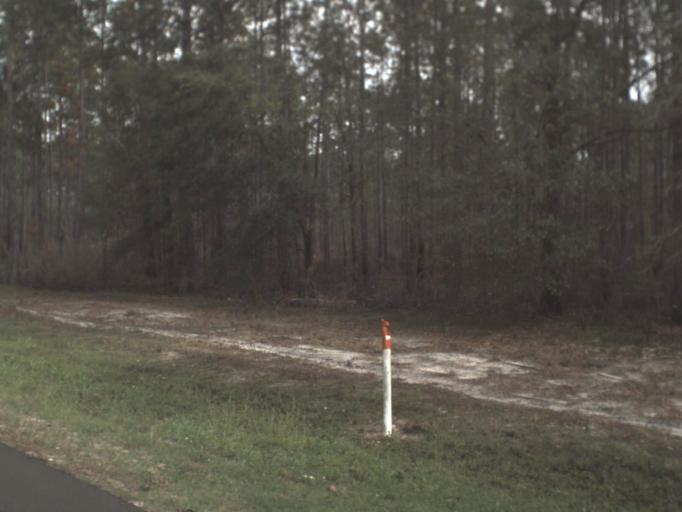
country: US
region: Florida
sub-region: Gadsden County
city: Midway
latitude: 30.4406
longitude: -84.4515
